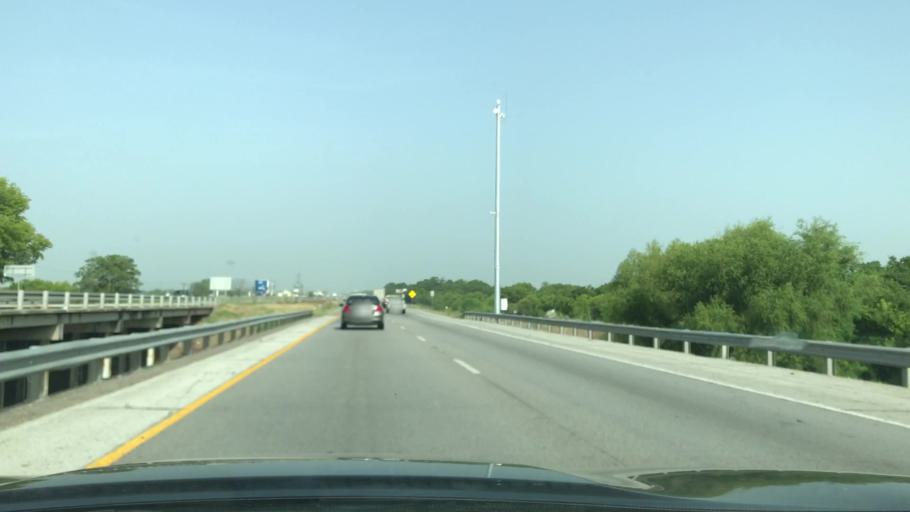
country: US
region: Texas
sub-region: Kaufman County
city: Forney
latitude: 32.7745
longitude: -96.5030
